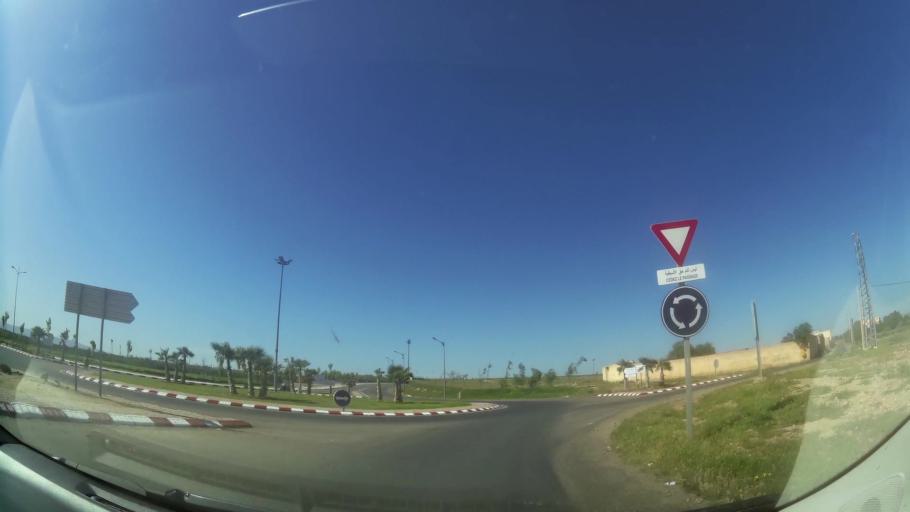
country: MA
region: Oriental
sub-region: Oujda-Angad
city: Oujda
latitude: 34.7369
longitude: -1.9189
